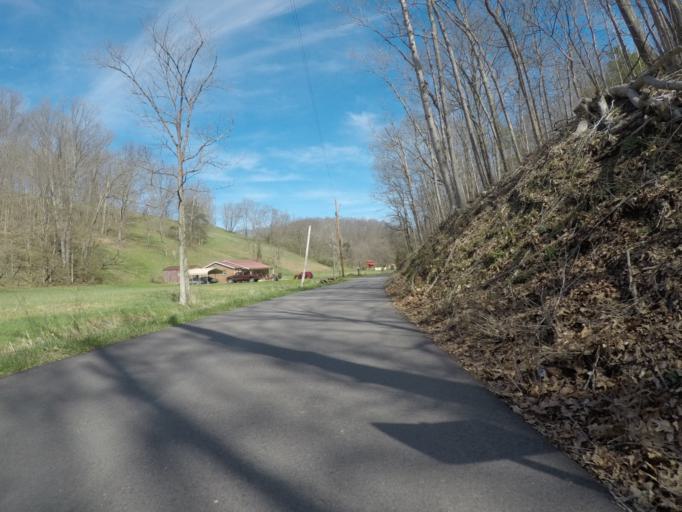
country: US
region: West Virginia
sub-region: Cabell County
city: Pea Ridge
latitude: 38.3959
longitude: -82.3511
